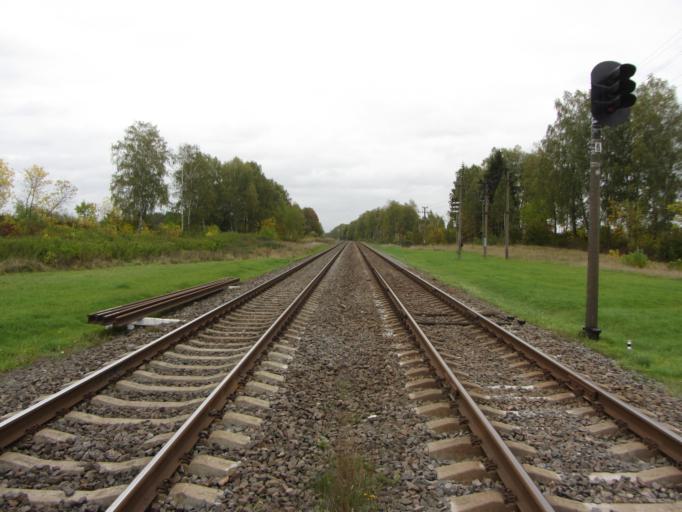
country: LT
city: Skaidiskes
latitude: 54.6524
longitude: 25.5755
